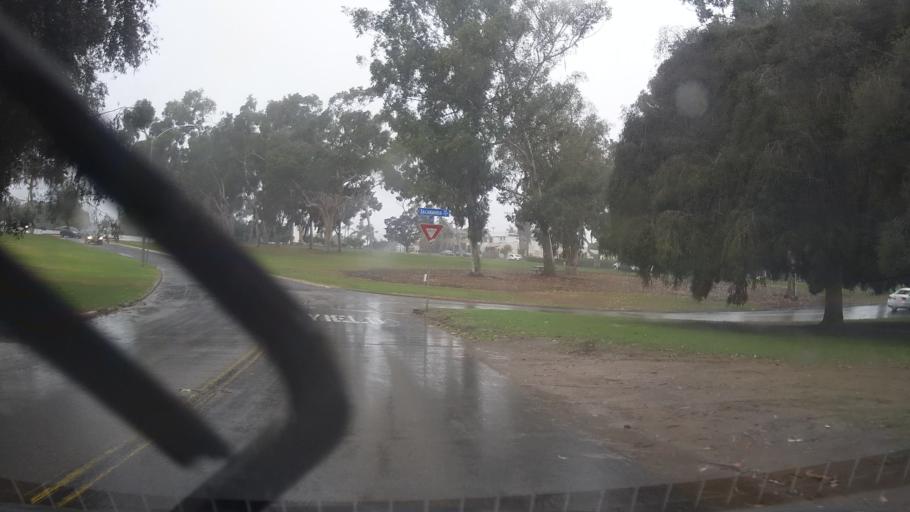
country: US
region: California
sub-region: San Diego County
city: San Diego
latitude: 32.7402
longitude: -117.1361
